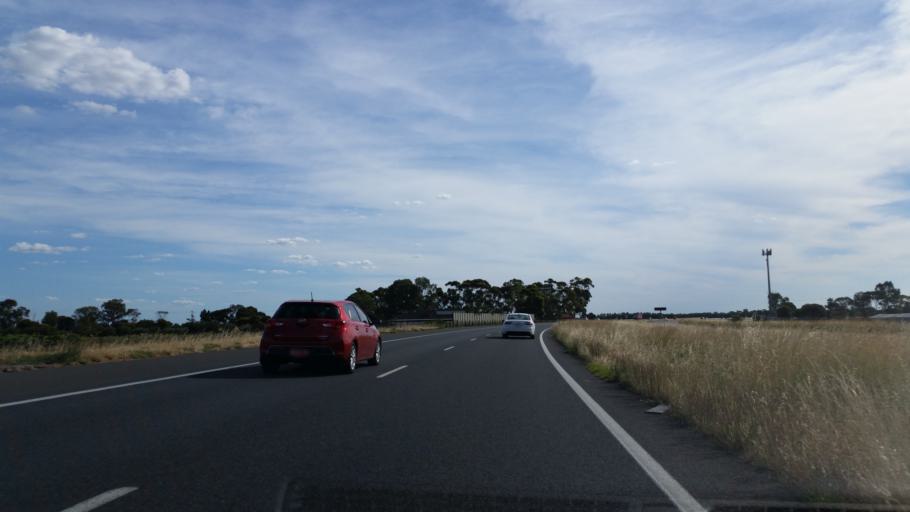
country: AU
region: South Australia
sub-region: Playford
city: Smithfield
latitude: -34.6788
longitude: 138.6478
